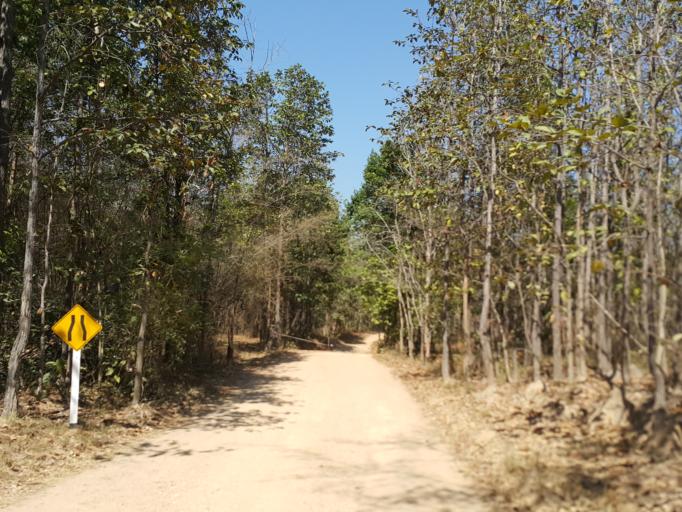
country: TH
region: Chiang Mai
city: Doi Lo
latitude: 18.5221
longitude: 98.7441
